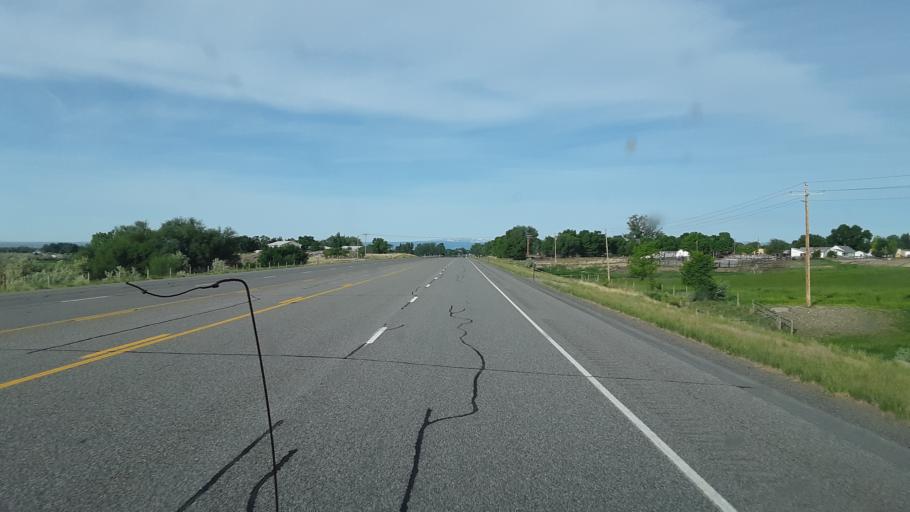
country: US
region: Wyoming
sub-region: Fremont County
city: Riverton
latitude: 43.1012
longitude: -108.3536
